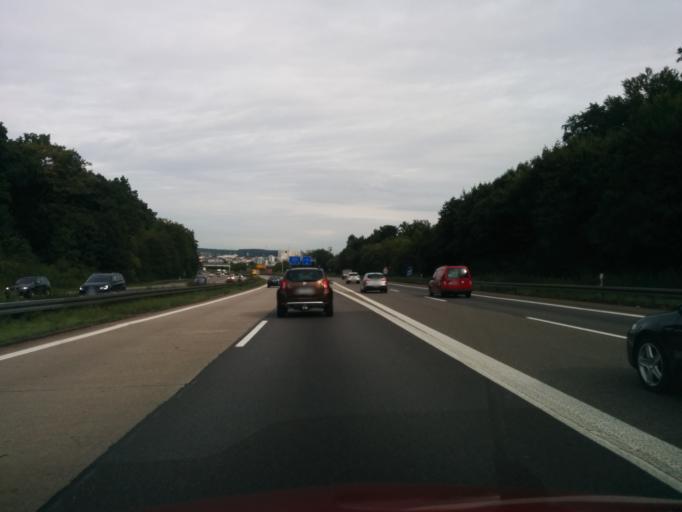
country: DE
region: Baden-Wuerttemberg
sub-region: Regierungsbezirk Stuttgart
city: Leonberg
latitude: 48.7712
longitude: 9.0288
